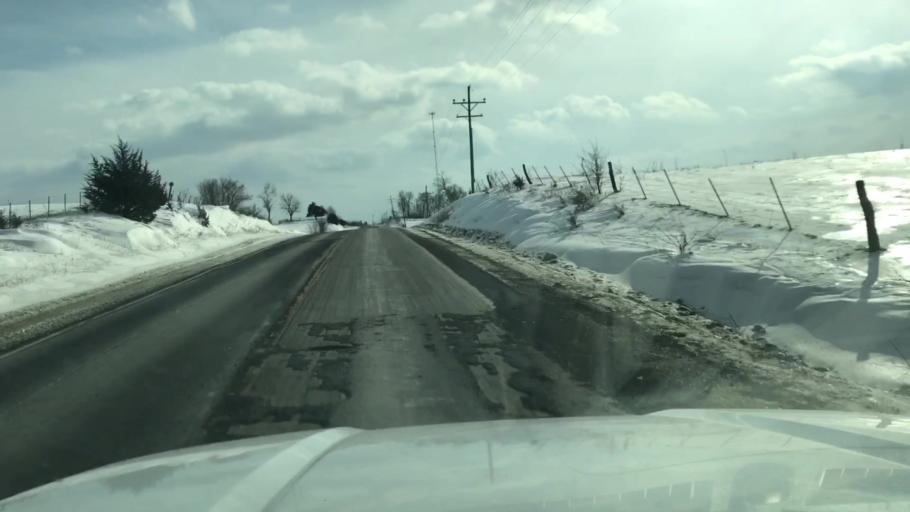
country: US
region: Missouri
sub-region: Gentry County
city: Stanberry
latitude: 40.3773
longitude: -94.6472
